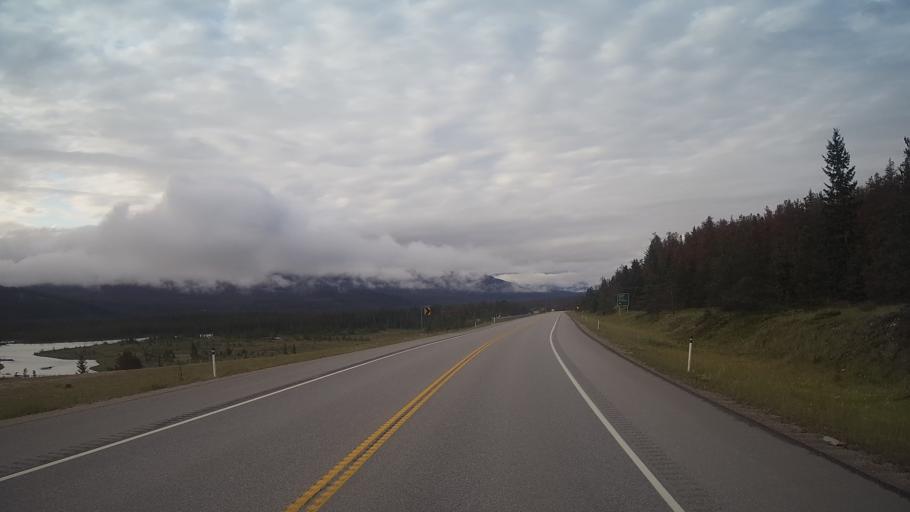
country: CA
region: Alberta
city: Jasper Park Lodge
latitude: 52.9470
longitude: -118.0394
